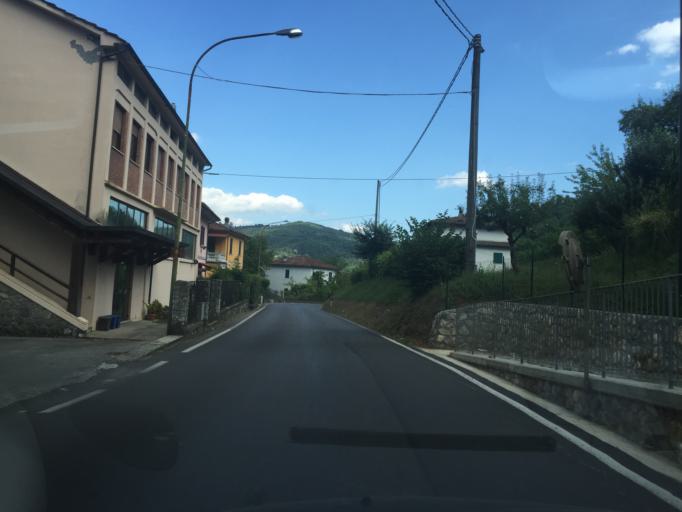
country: IT
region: Tuscany
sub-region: Provincia di Lucca
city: Castelnuovo di Garfagnana
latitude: 44.1149
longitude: 10.3984
